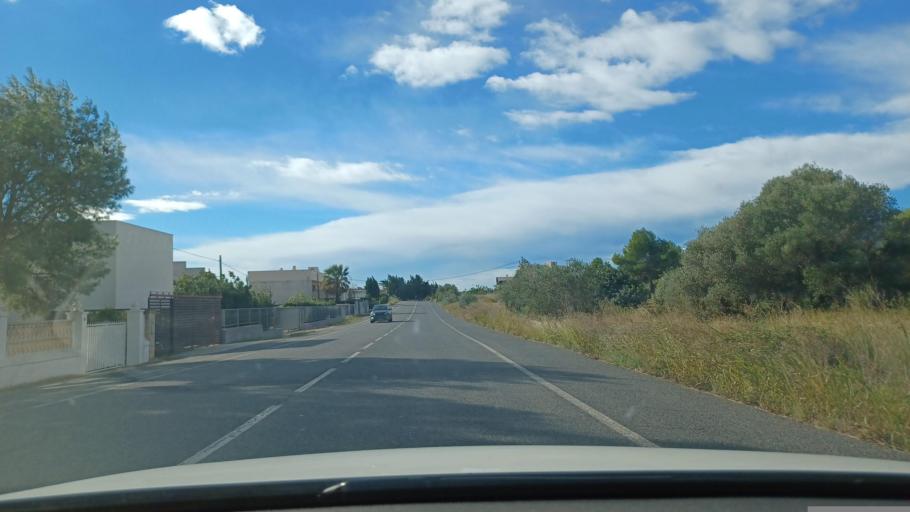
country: ES
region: Catalonia
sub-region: Provincia de Tarragona
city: Sant Carles de la Rapita
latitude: 40.5926
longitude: 0.5670
